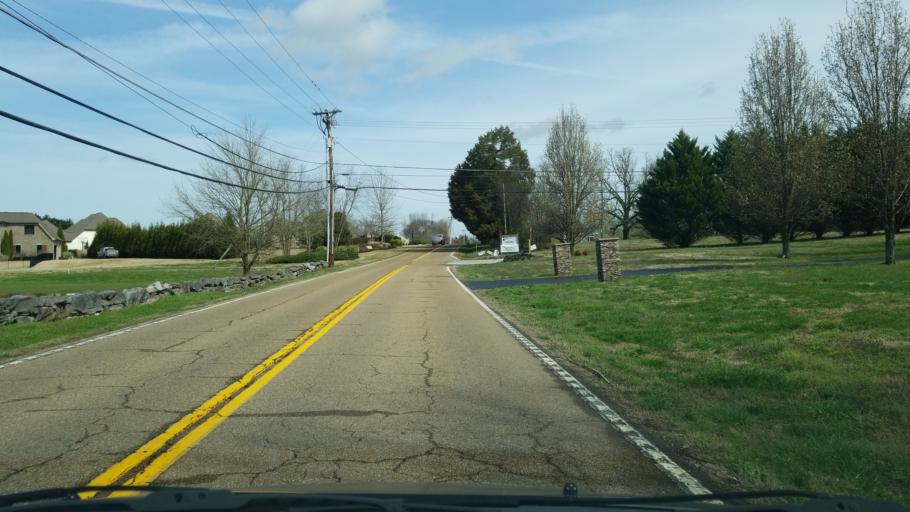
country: US
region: Tennessee
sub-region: Hamilton County
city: Harrison
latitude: 35.1455
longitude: -85.0631
